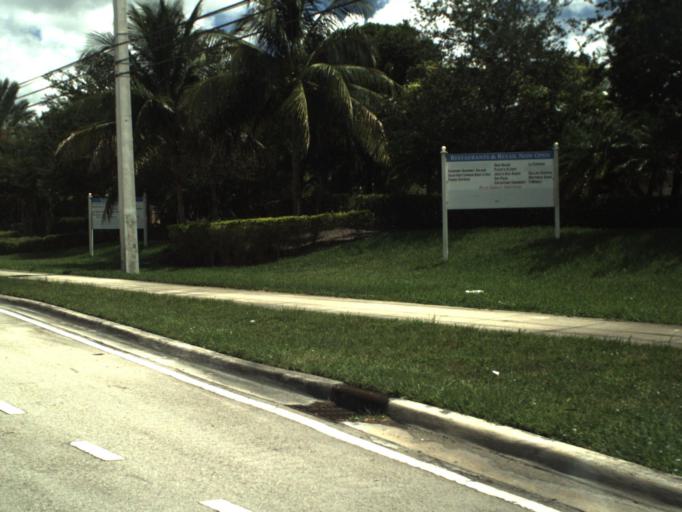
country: US
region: Florida
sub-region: Miami-Dade County
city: Country Club
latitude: 25.9787
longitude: -80.3096
